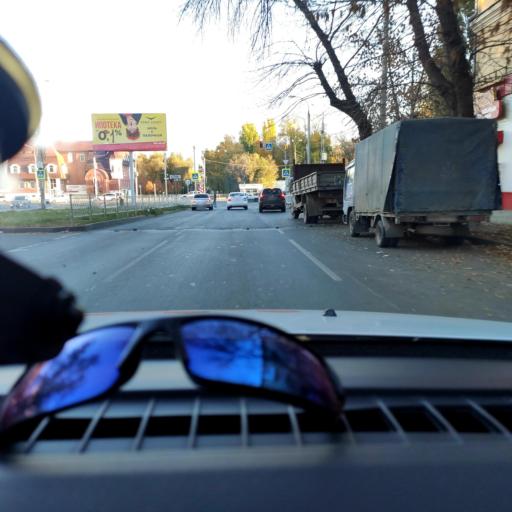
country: RU
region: Samara
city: Samara
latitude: 53.2134
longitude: 50.2475
